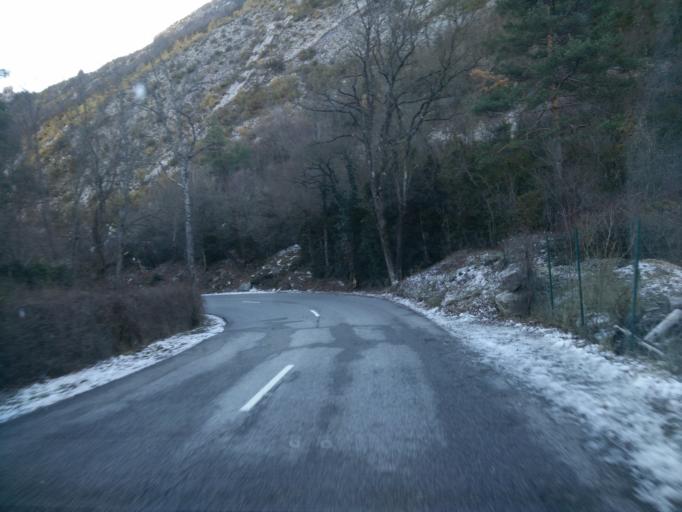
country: FR
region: Provence-Alpes-Cote d'Azur
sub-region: Departement des Alpes-de-Haute-Provence
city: Castellane
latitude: 43.8215
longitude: 6.4313
